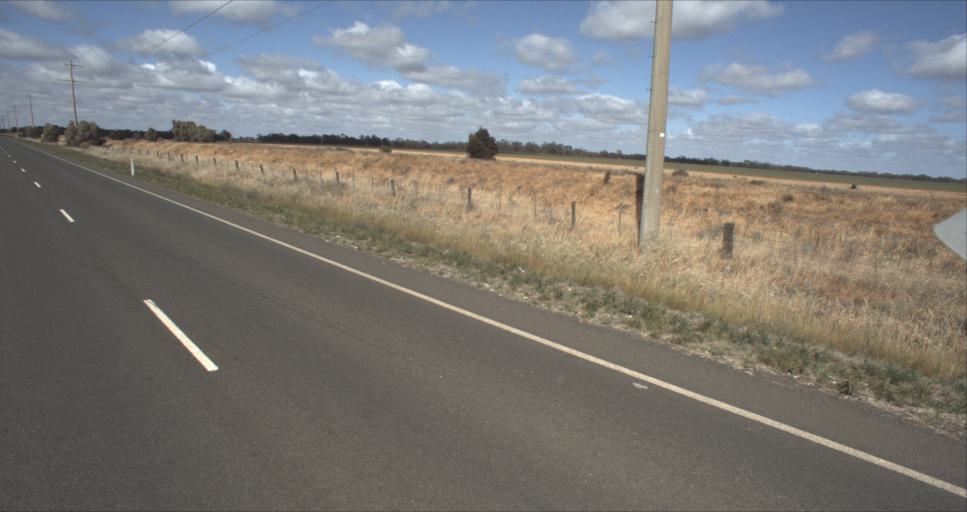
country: AU
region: New South Wales
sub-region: Murrumbidgee Shire
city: Darlington Point
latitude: -34.5329
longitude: 146.1736
